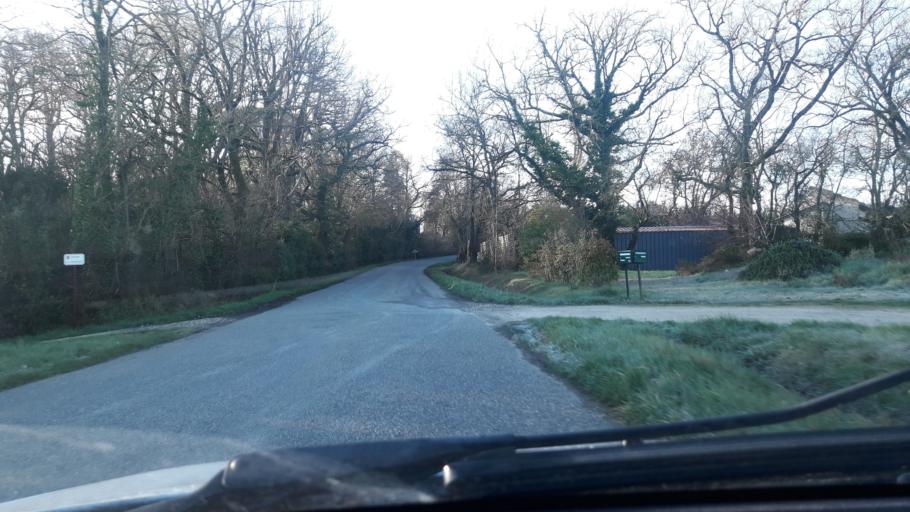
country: FR
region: Midi-Pyrenees
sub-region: Departement du Gers
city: Gimont
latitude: 43.6438
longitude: 0.9978
